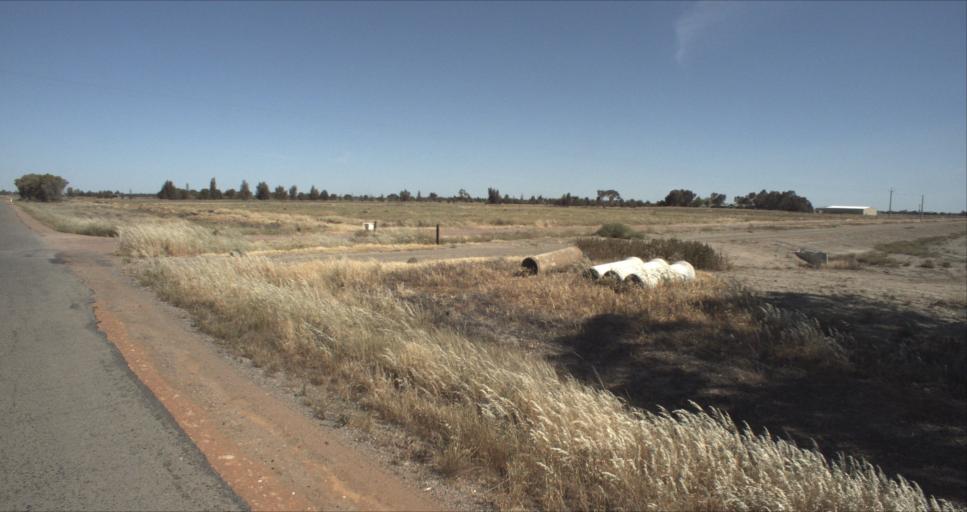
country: AU
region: New South Wales
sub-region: Leeton
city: Leeton
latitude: -34.4845
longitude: 146.3754
